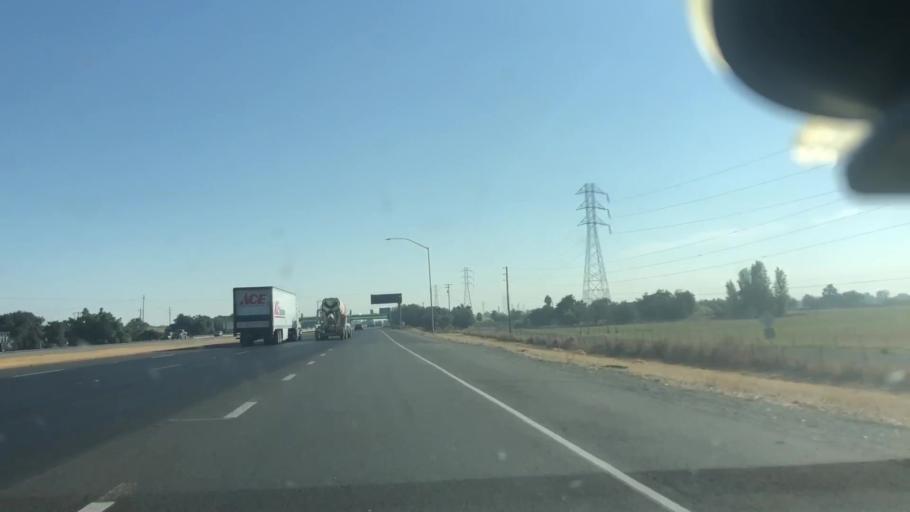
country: US
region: California
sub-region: San Joaquin County
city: Lathrop
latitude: 37.7630
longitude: -121.3370
